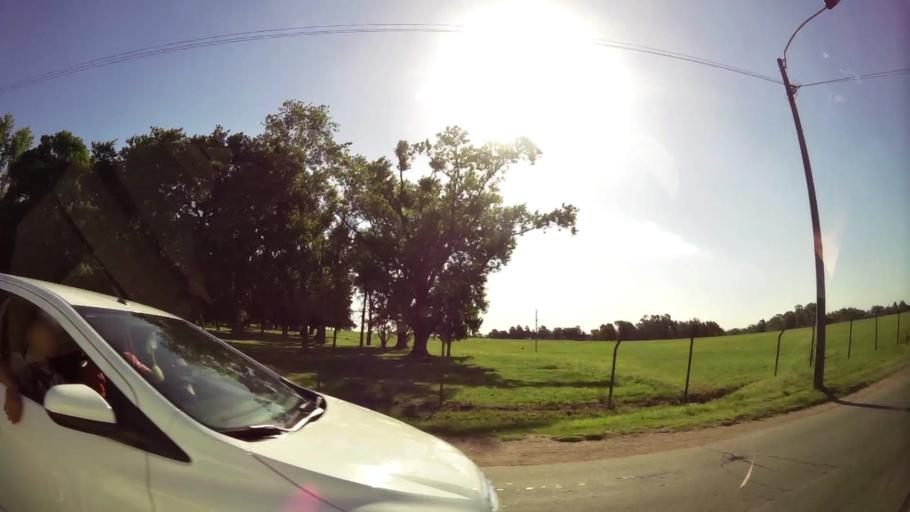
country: UY
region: Canelones
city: La Paz
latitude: -34.8105
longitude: -56.1599
